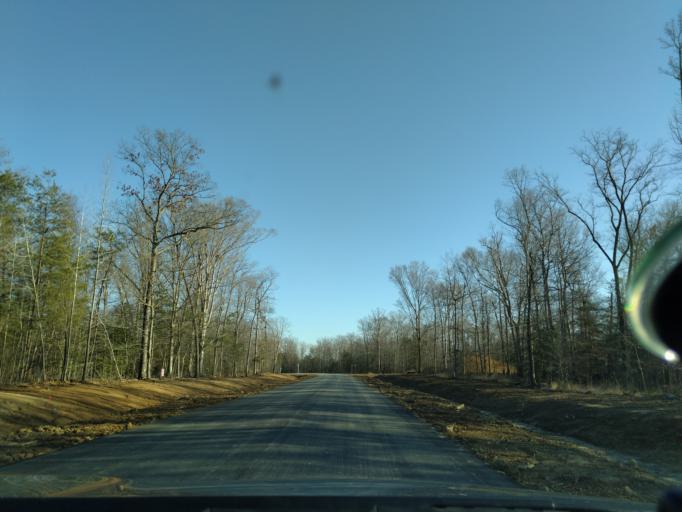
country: US
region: Maryland
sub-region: Charles County
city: La Plata
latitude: 38.4922
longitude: -76.8914
